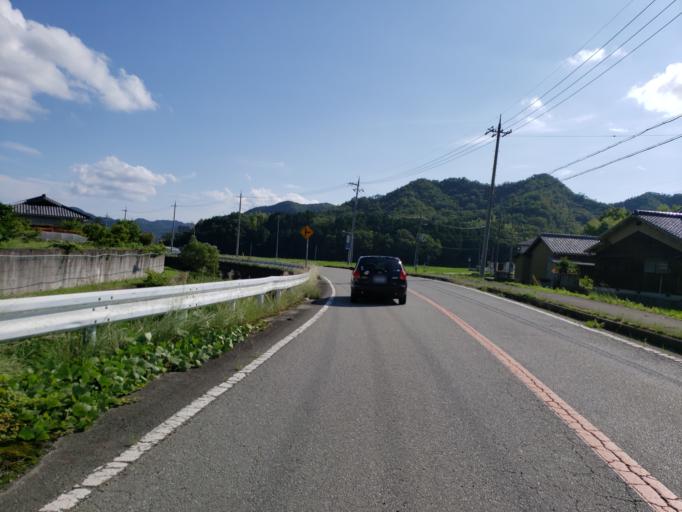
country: JP
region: Hyogo
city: Kakogawacho-honmachi
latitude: 34.8786
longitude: 134.7988
